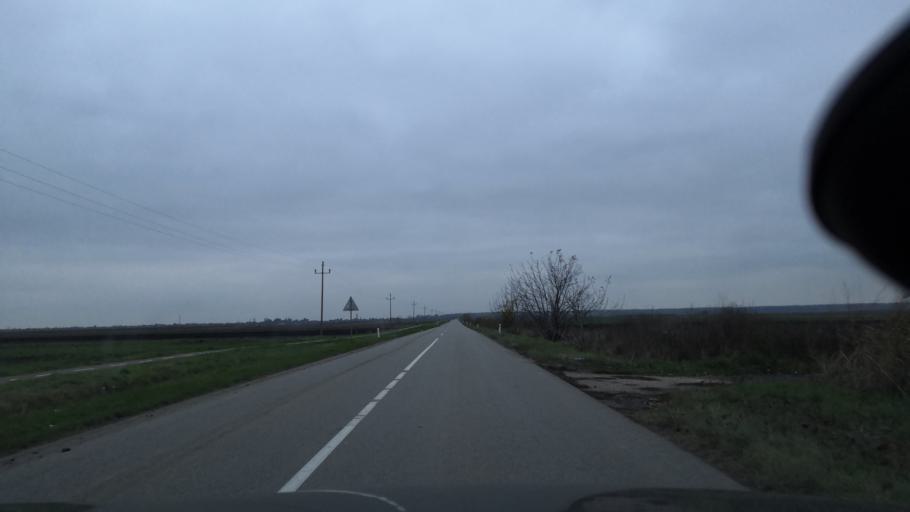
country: HU
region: Csongrad
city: Roszke
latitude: 46.1482
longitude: 20.1022
